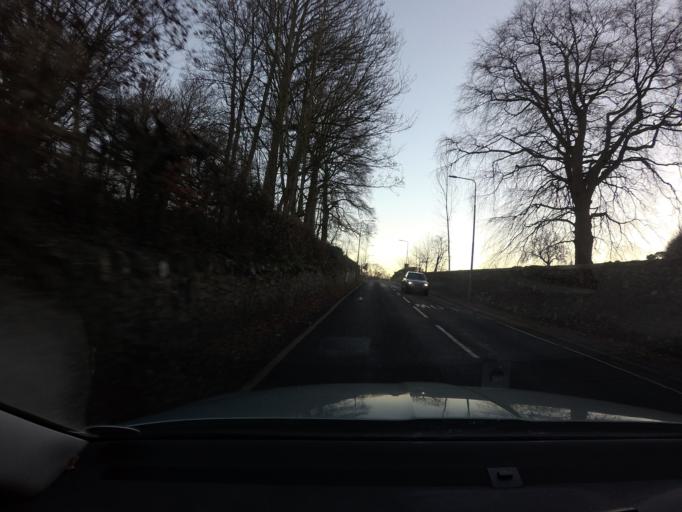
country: GB
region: Scotland
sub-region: Fife
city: Newport-On-Tay
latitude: 56.4352
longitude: -2.9367
